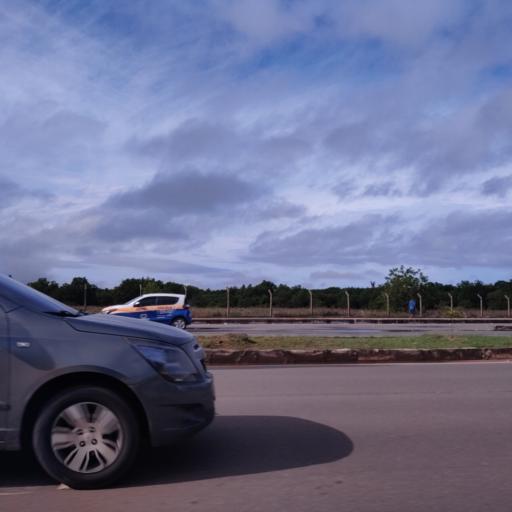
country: BR
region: Maranhao
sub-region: Sao Luis
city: Sao Luis
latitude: -2.5121
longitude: -44.2733
